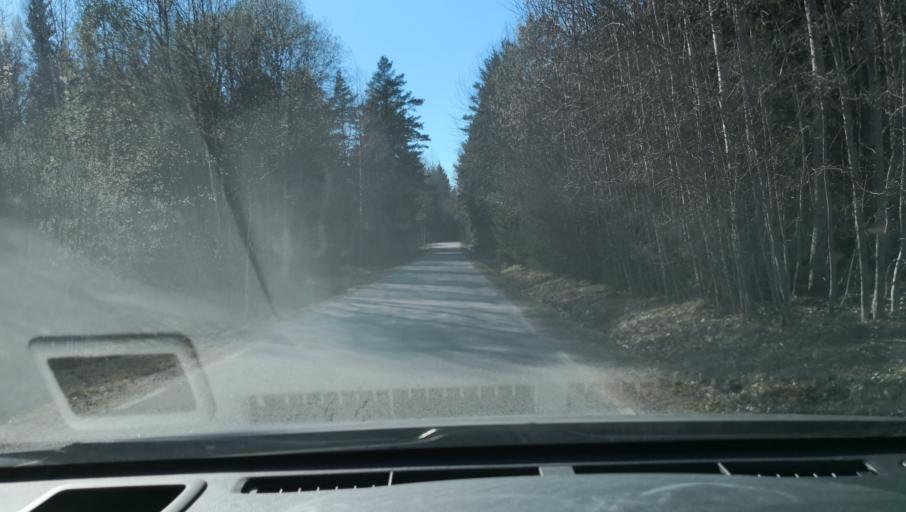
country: SE
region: Dalarna
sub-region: Avesta Kommun
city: Horndal
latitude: 60.0824
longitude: 16.4449
